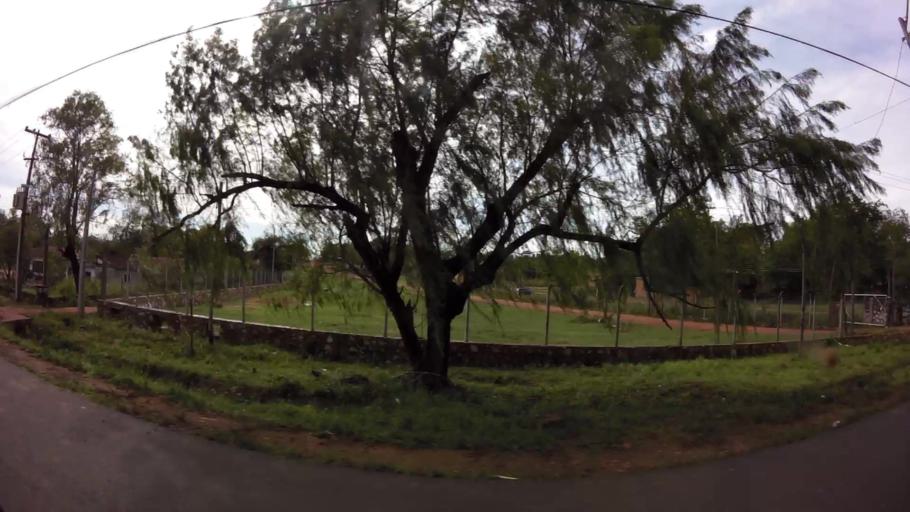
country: PY
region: Central
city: Limpio
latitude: -25.1417
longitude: -57.4567
